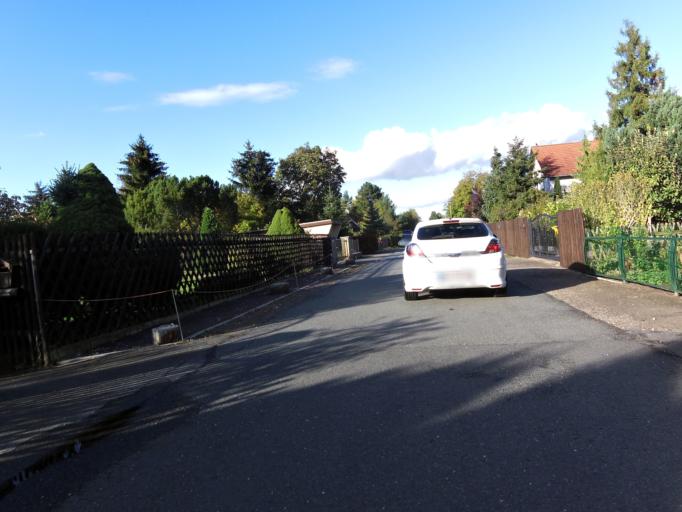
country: DE
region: Saxony
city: Grossposna
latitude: 51.3188
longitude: 12.4739
